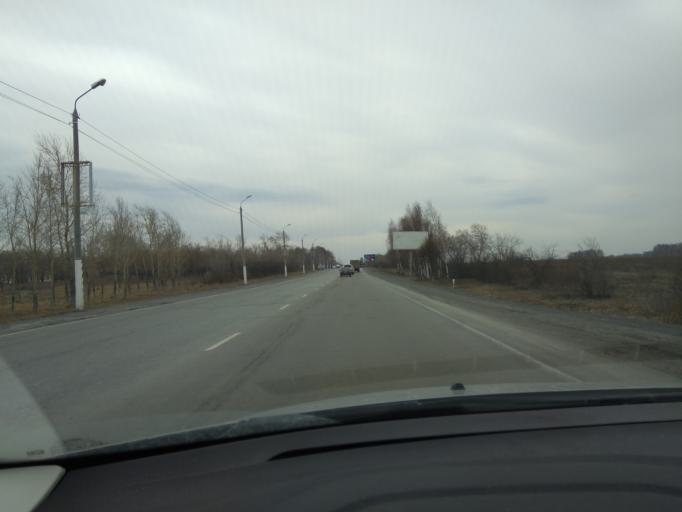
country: RU
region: Chelyabinsk
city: Potanino
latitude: 55.2931
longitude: 61.5113
